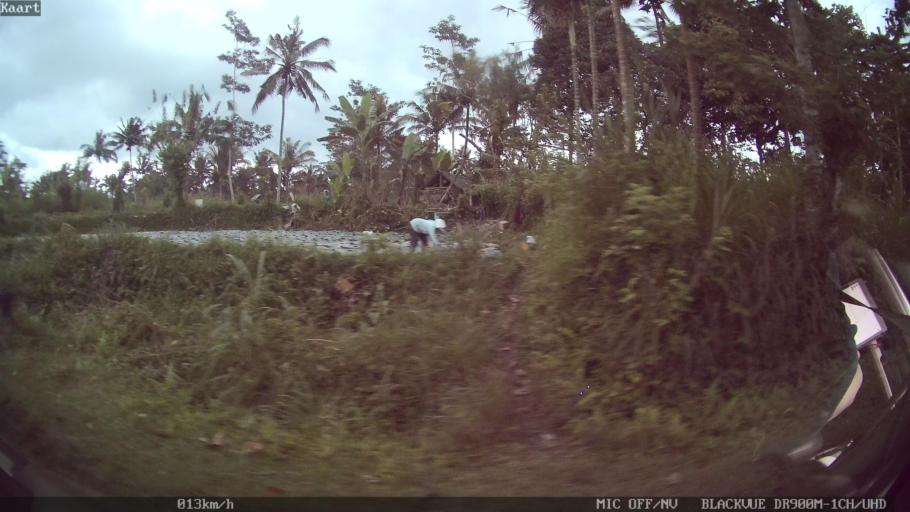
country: ID
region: Bali
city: Banjar Wangsian
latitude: -8.4403
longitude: 115.4262
